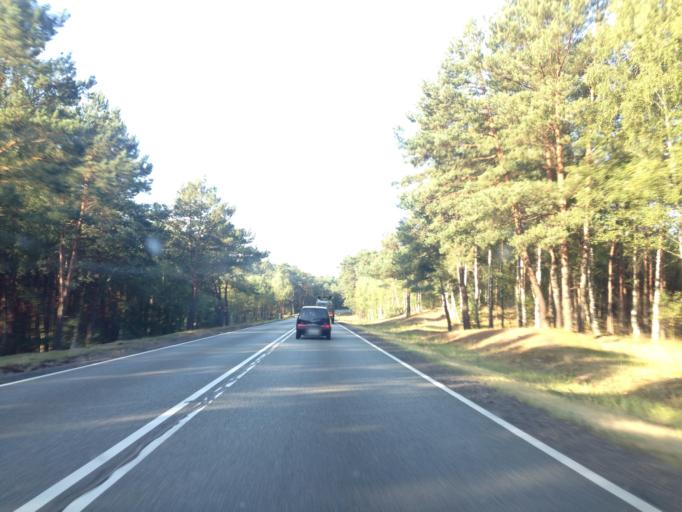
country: PL
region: Kujawsko-Pomorskie
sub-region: Powiat bydgoski
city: Nowa Wies Wielka
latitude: 53.0561
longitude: 18.0658
